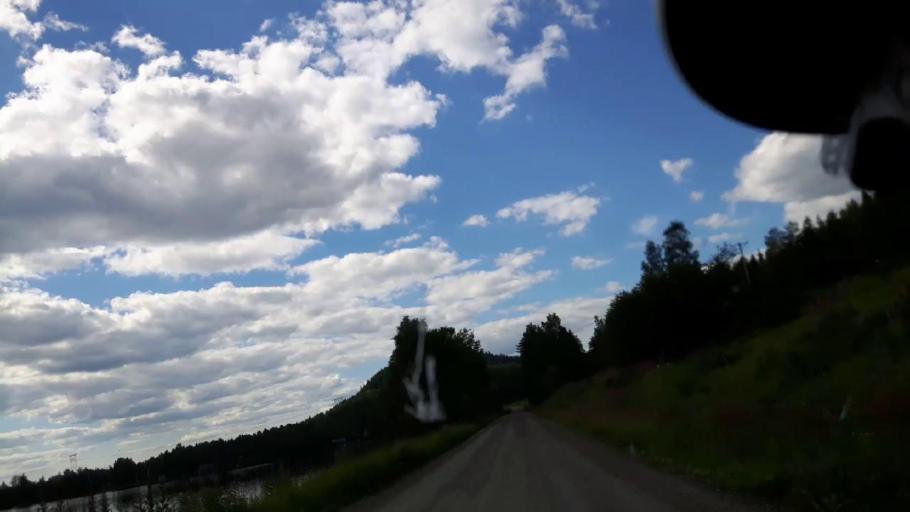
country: SE
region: Jaemtland
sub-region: Braecke Kommun
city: Braecke
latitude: 62.7179
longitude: 15.5907
